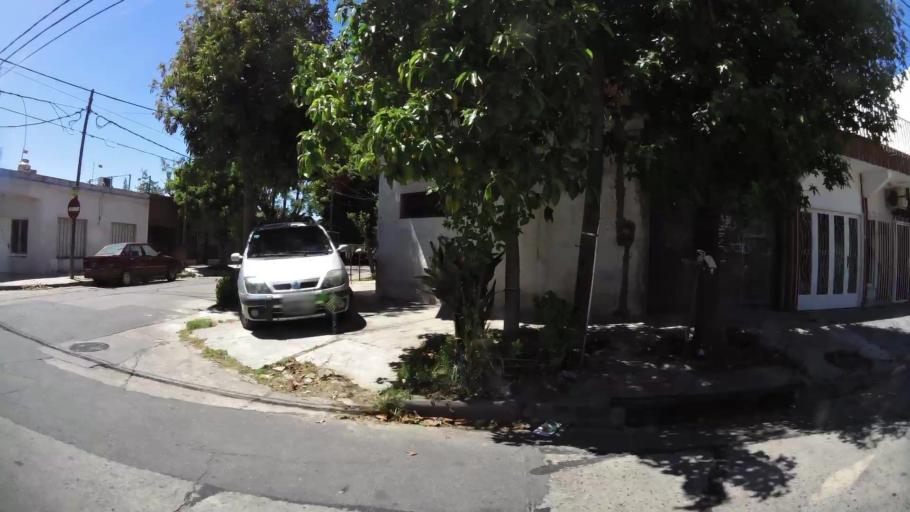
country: AR
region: Buenos Aires
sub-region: Partido de San Isidro
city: San Isidro
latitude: -34.5054
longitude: -58.5470
